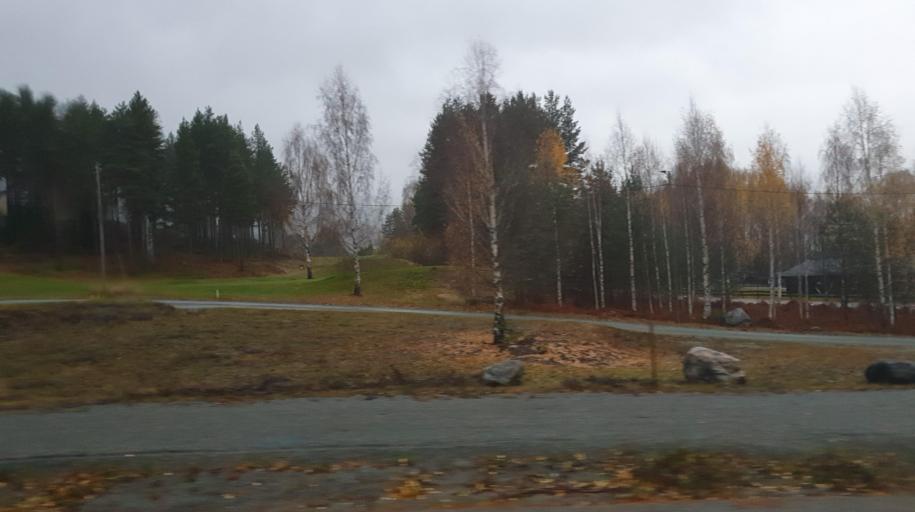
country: NO
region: Buskerud
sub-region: Krodsherad
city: Noresund
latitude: 60.1887
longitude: 9.6061
